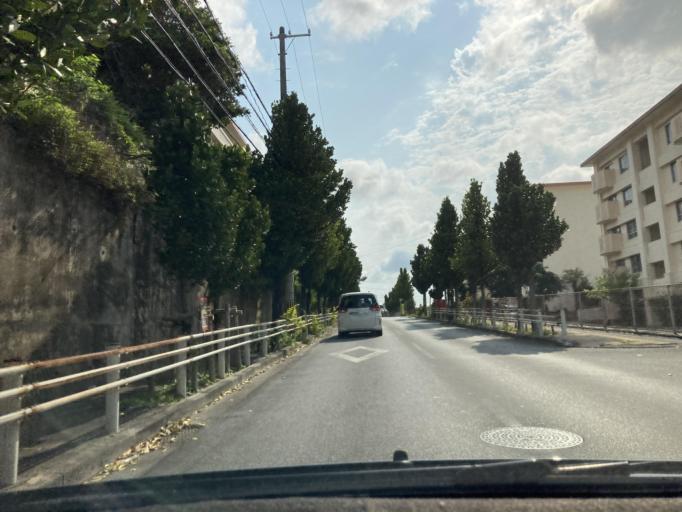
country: JP
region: Okinawa
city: Tomigusuku
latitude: 26.1987
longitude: 127.7198
